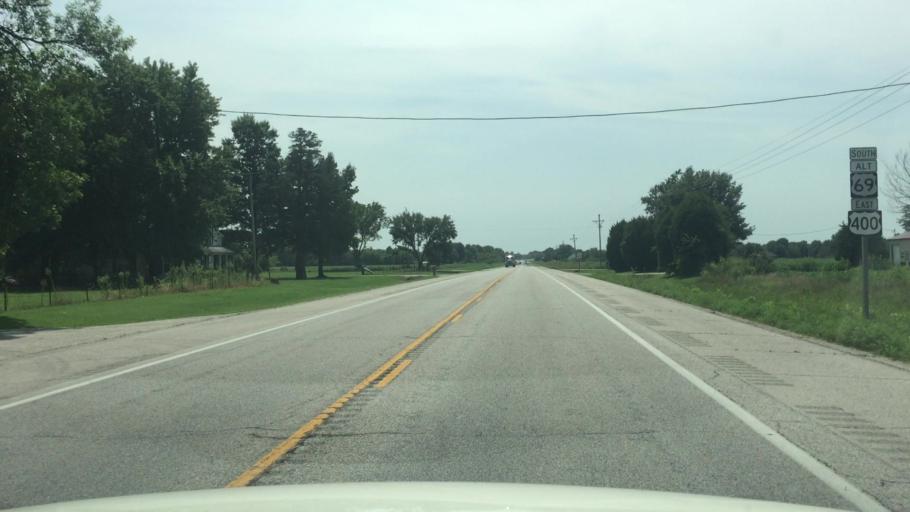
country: US
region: Kansas
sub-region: Cherokee County
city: Galena
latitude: 37.1025
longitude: -94.7044
